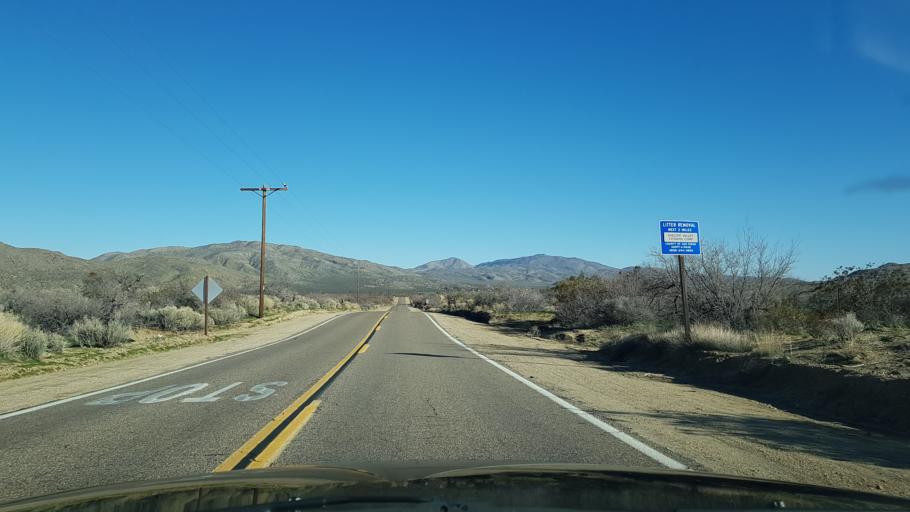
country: US
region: California
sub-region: San Diego County
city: Julian
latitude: 33.0963
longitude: -116.4738
